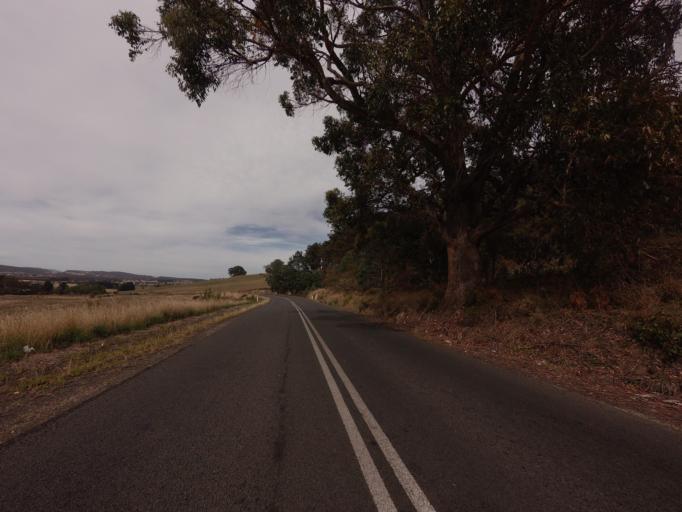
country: AU
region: Tasmania
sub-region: Sorell
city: Sorell
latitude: -42.4220
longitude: 147.4648
